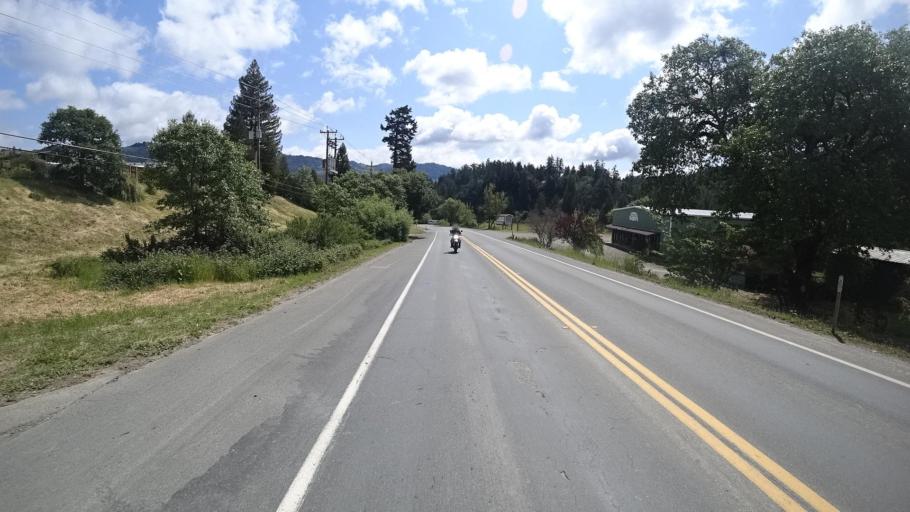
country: US
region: California
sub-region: Humboldt County
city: Redway
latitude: 40.1157
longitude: -123.8152
